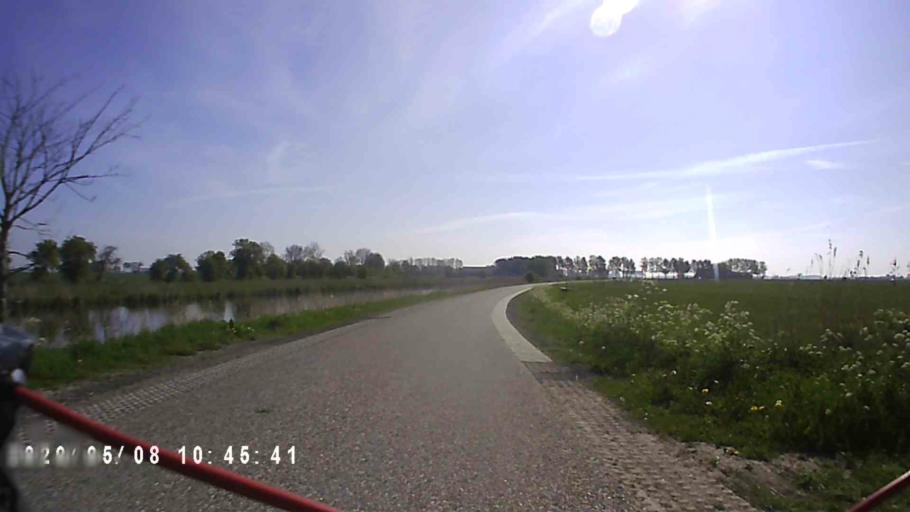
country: NL
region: Groningen
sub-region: Gemeente Winsum
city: Winsum
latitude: 53.3347
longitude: 6.5357
